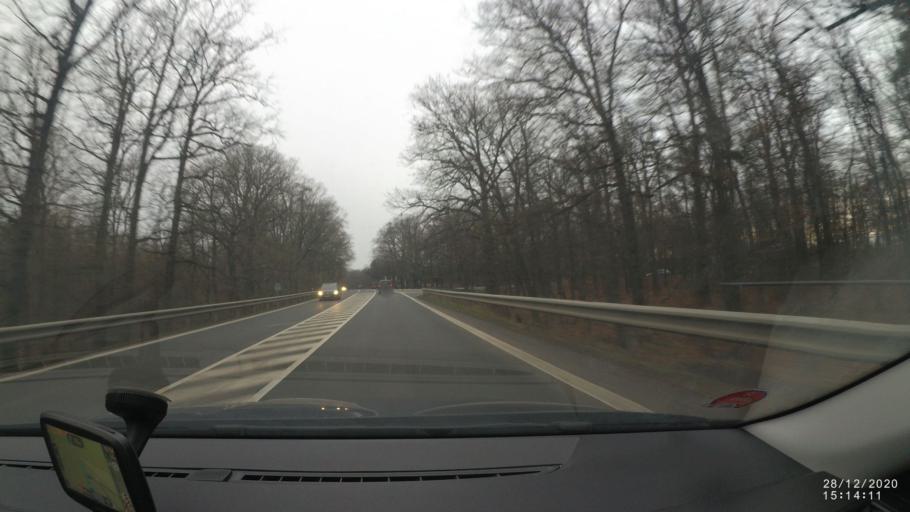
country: CZ
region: Central Bohemia
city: Uvaly
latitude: 50.0718
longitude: 14.7045
